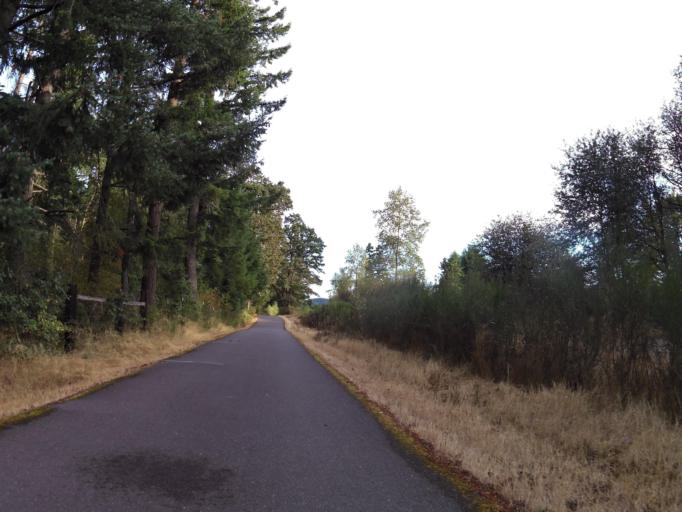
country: US
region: Washington
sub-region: Thurston County
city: Tenino
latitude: 46.9163
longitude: -122.7990
